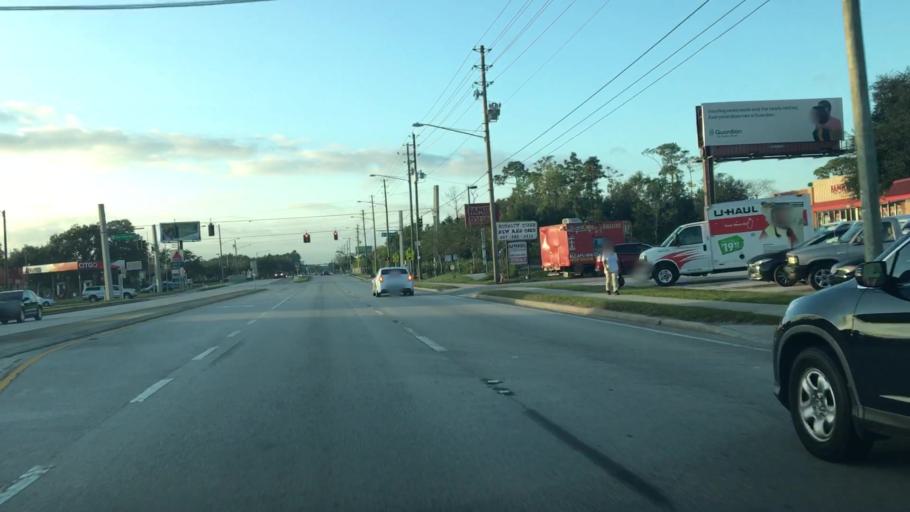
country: US
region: Florida
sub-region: Orange County
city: Conway
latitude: 28.4935
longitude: -81.2855
